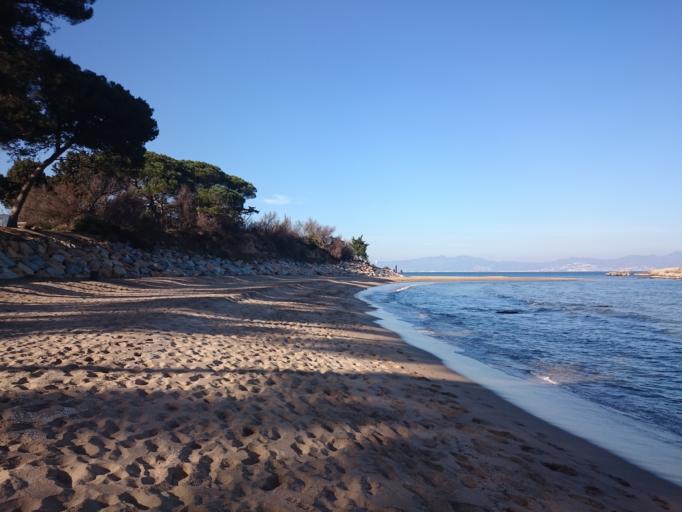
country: ES
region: Catalonia
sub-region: Provincia de Girona
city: l'Escala
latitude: 42.1341
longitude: 3.1218
